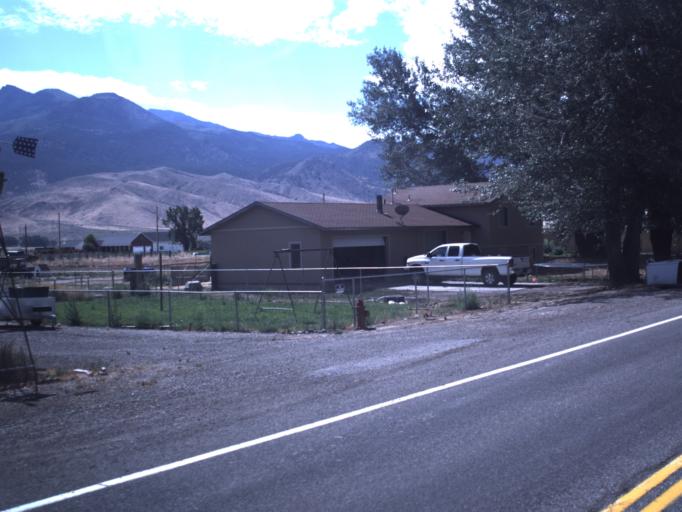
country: US
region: Utah
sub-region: Sevier County
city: Monroe
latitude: 38.6706
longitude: -112.1210
